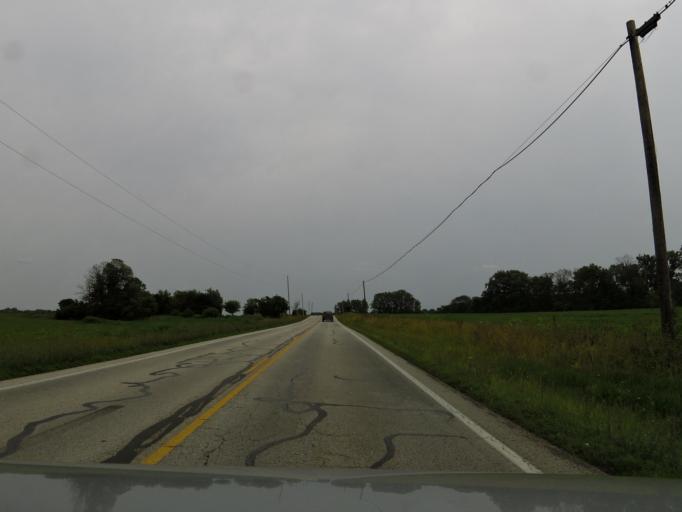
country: US
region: Ohio
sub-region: Warren County
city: Waynesville
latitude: 39.4947
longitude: -83.9733
